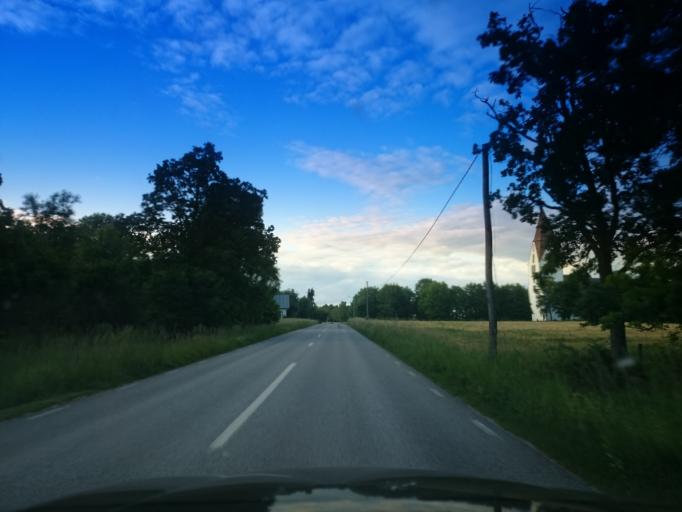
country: SE
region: Gotland
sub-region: Gotland
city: Hemse
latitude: 57.3115
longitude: 18.3815
